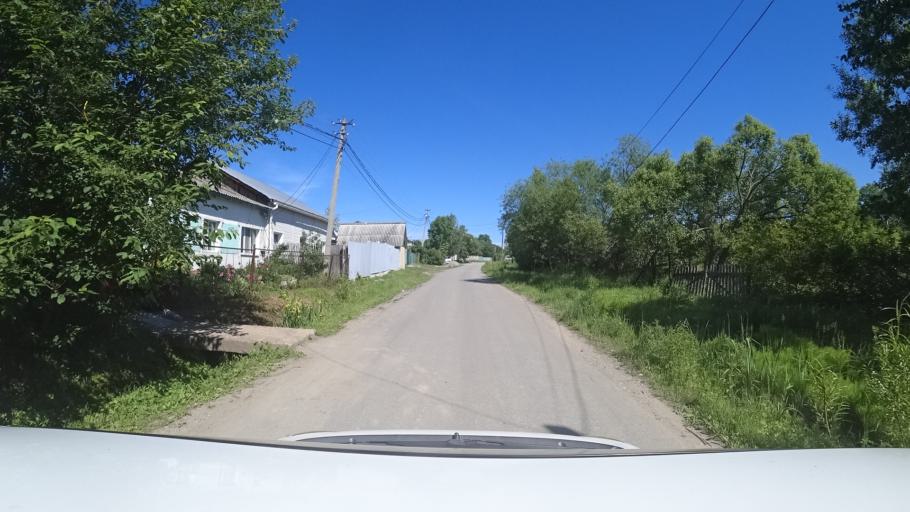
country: RU
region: Khabarovsk Krai
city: Topolevo
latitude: 48.5560
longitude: 135.1879
